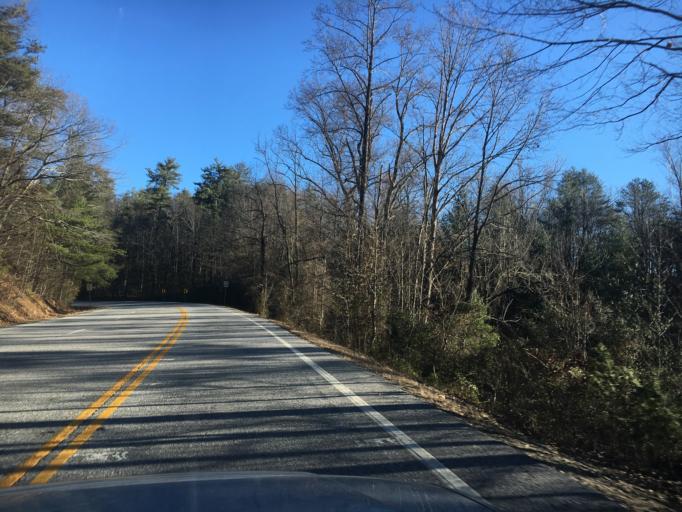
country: US
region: Georgia
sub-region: White County
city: Cleveland
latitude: 34.6869
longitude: -83.9070
